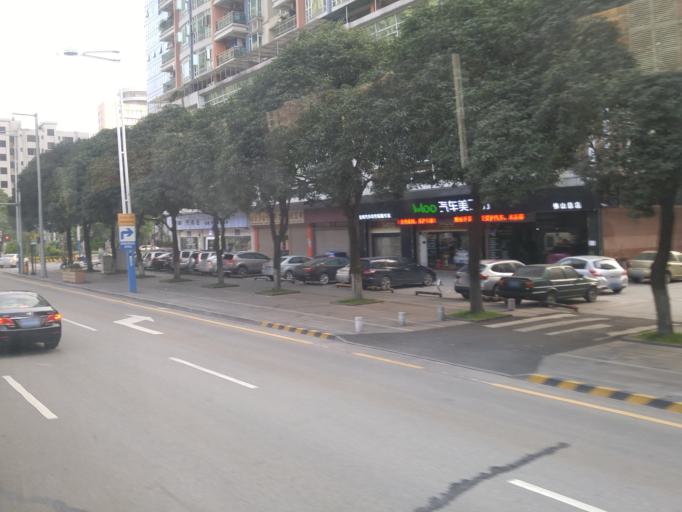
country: CN
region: Guangdong
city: Foshan
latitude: 23.0617
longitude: 113.1401
